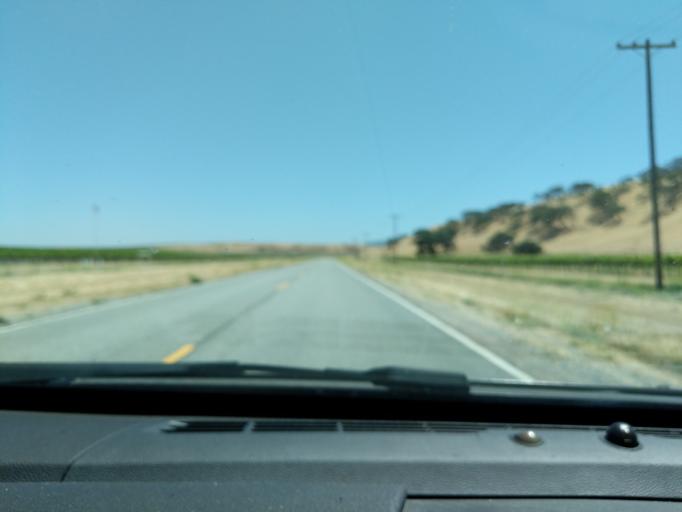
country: US
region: California
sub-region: Monterey County
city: King City
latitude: 36.1747
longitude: -121.1321
